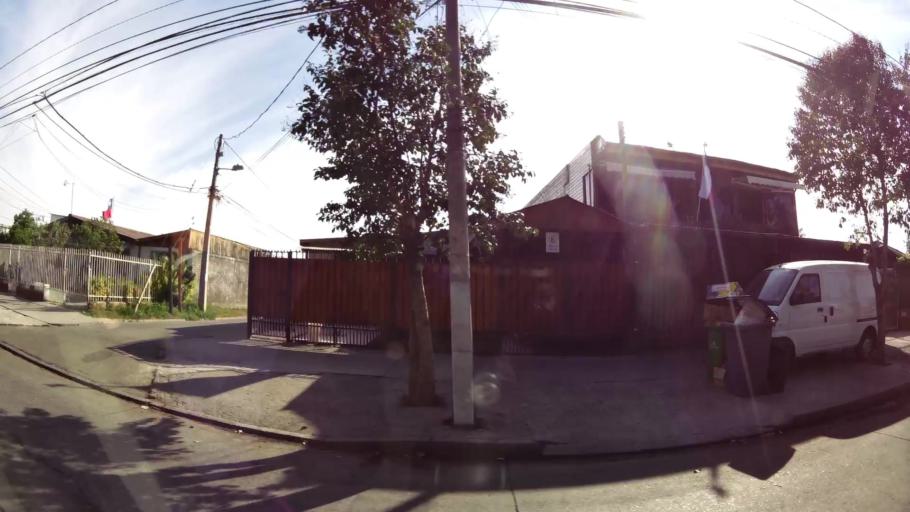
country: CL
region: Santiago Metropolitan
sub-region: Provincia de Cordillera
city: Puente Alto
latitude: -33.6288
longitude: -70.5899
